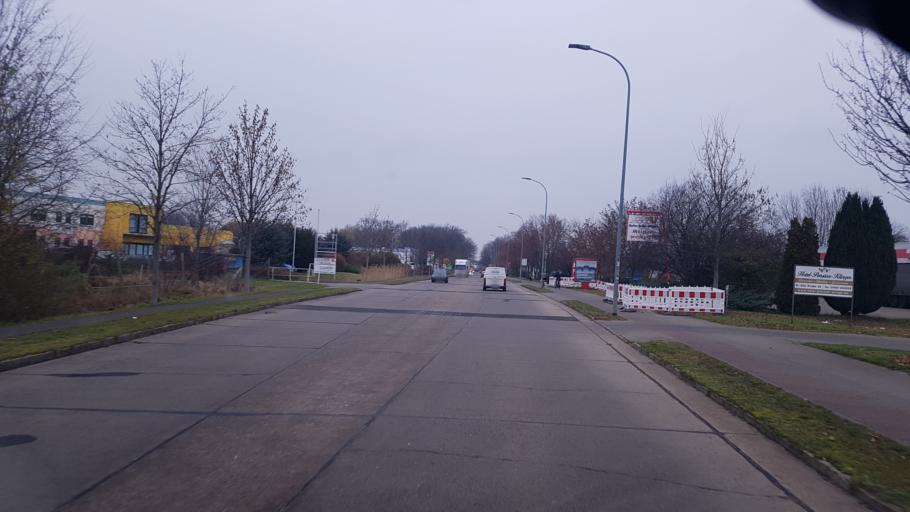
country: DE
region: Brandenburg
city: Guben
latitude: 51.9535
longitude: 14.7026
